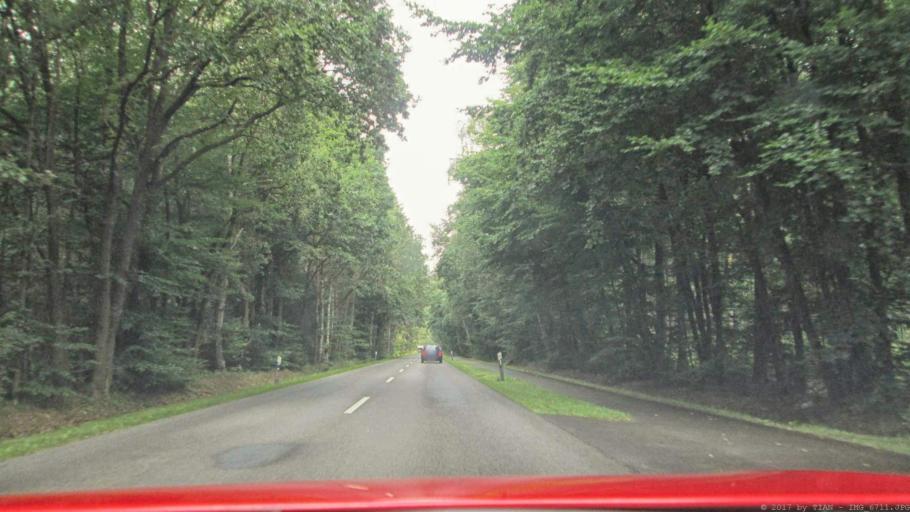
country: DE
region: Lower Saxony
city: Emmendorf
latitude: 52.9974
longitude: 10.5850
